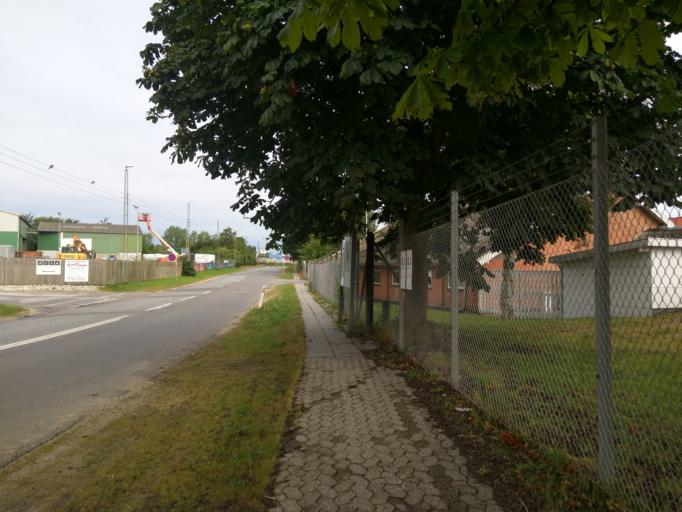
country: DK
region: Central Jutland
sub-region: Viborg Kommune
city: Viborg
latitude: 56.4497
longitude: 9.3832
